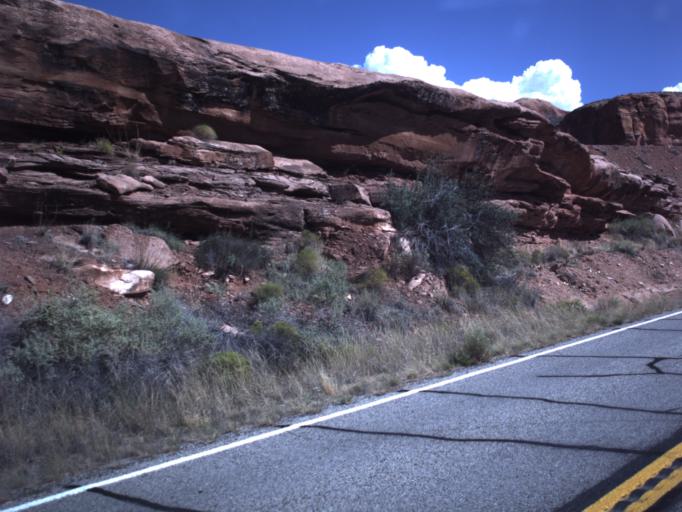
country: US
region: Utah
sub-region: Grand County
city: Moab
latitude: 38.5776
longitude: -109.6352
